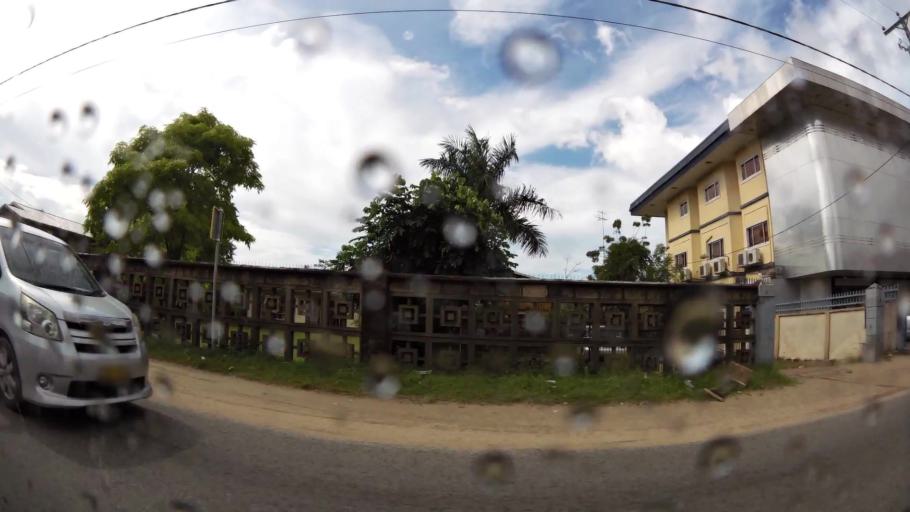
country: SR
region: Paramaribo
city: Paramaribo
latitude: 5.8420
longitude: -55.1970
